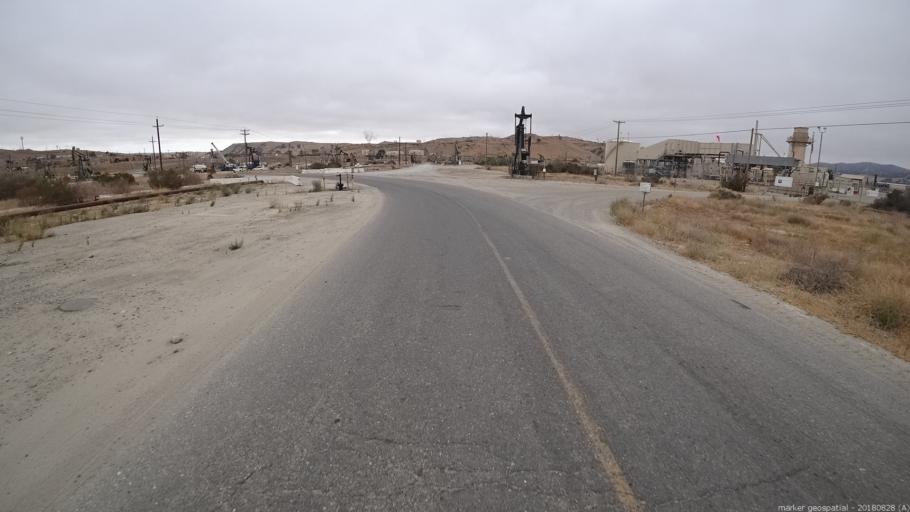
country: US
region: California
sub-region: San Luis Obispo County
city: Lake Nacimiento
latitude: 35.9526
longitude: -120.8682
